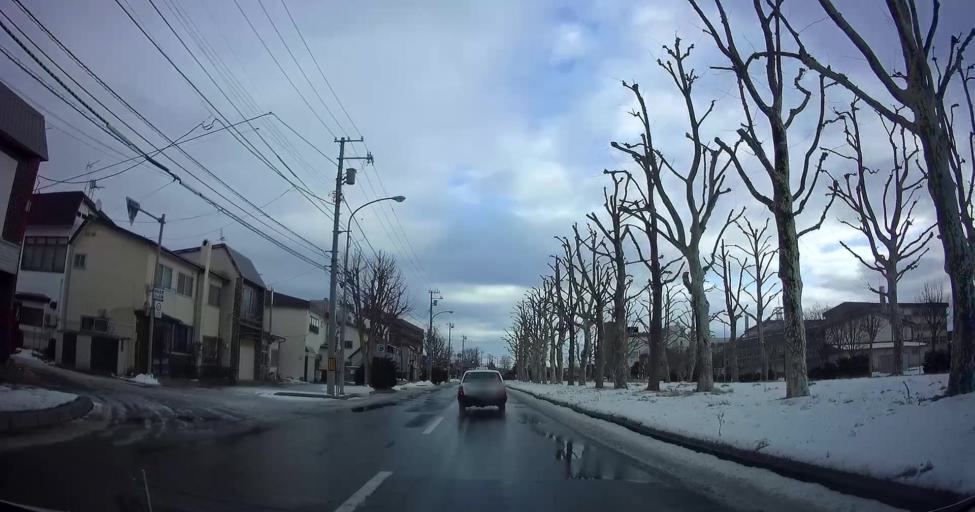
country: JP
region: Hokkaido
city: Hakodate
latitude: 41.7793
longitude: 140.7362
